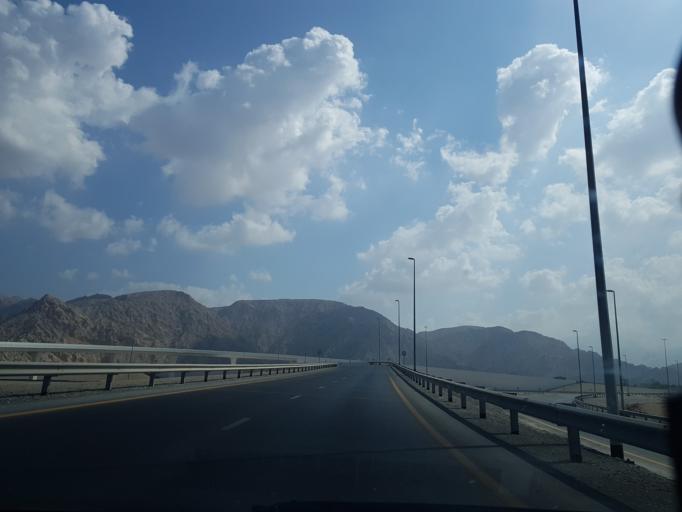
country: AE
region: Ra's al Khaymah
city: Ras al-Khaimah
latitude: 25.8329
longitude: 56.0130
